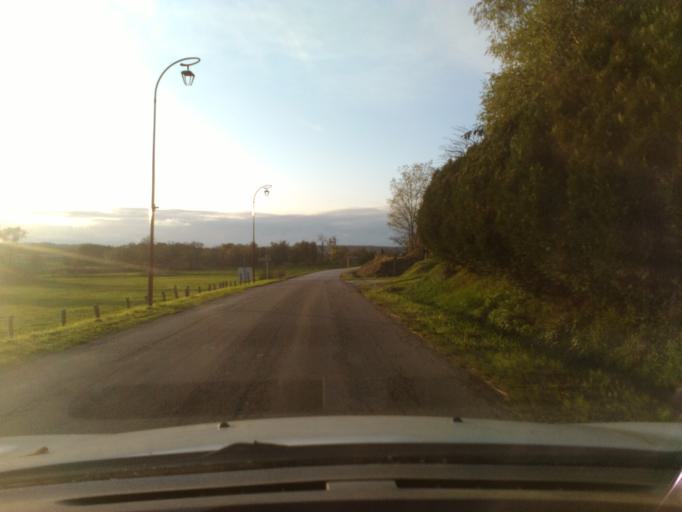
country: FR
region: Lorraine
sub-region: Departement des Vosges
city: Mirecourt
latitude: 48.2580
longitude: 6.1847
